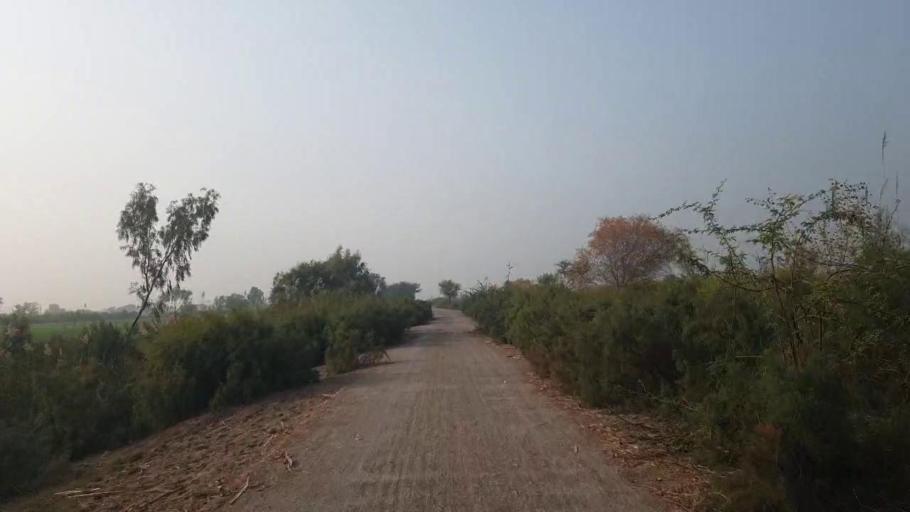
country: PK
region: Sindh
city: Shahdadpur
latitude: 25.8522
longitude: 68.5948
